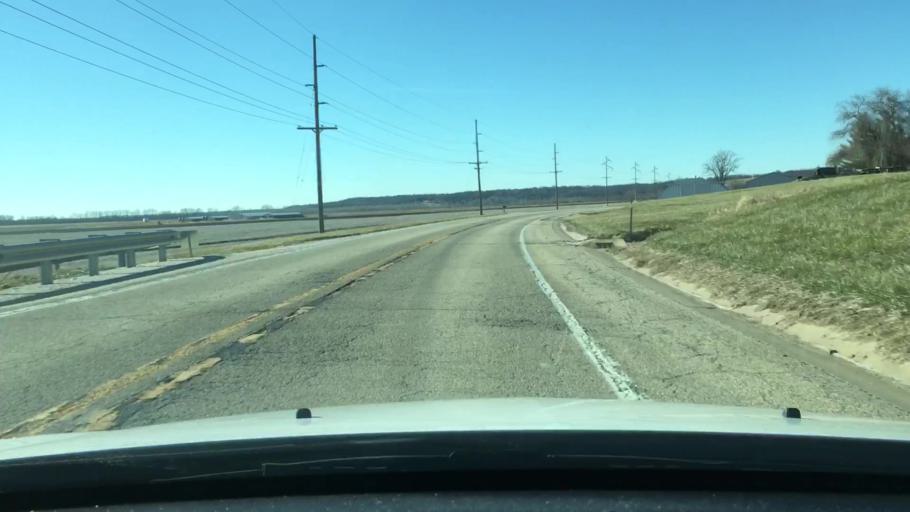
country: US
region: Illinois
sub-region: Fulton County
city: Astoria
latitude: 40.1755
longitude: -90.2582
